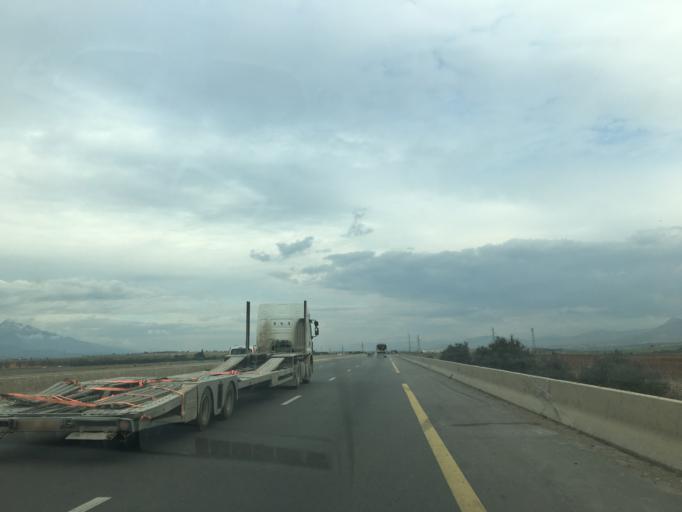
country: DZ
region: Bouira
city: Bouira
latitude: 36.3275
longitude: 3.9751
